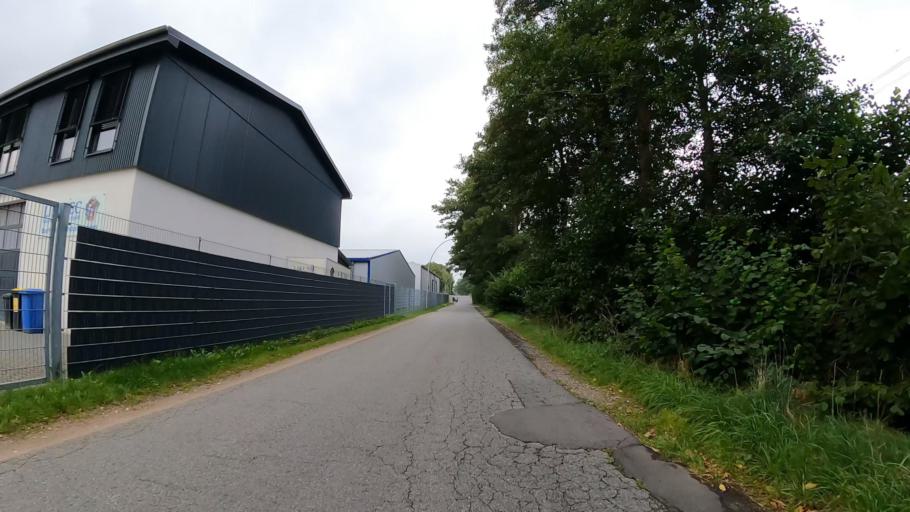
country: DE
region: Schleswig-Holstein
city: Halstenbek
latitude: 53.6188
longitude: 9.8603
